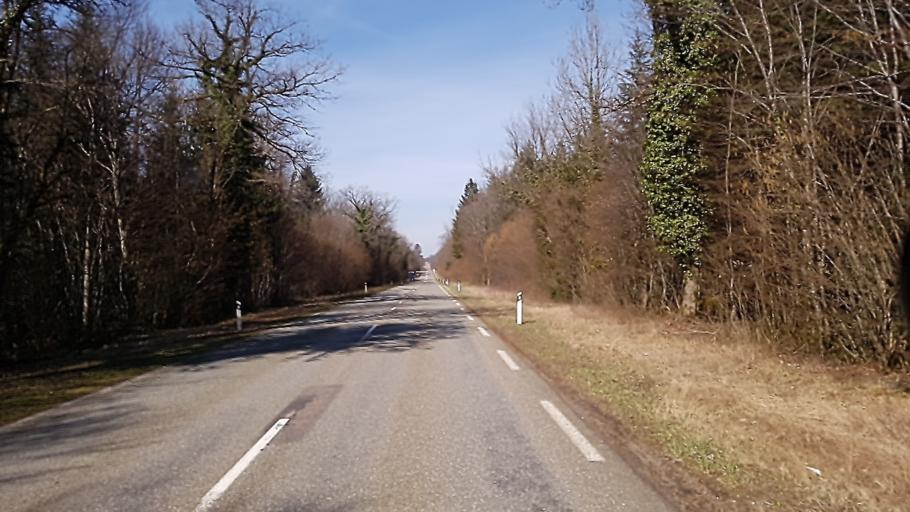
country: FR
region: Franche-Comte
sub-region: Departement du Jura
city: Poligny
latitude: 46.8118
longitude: 5.7949
